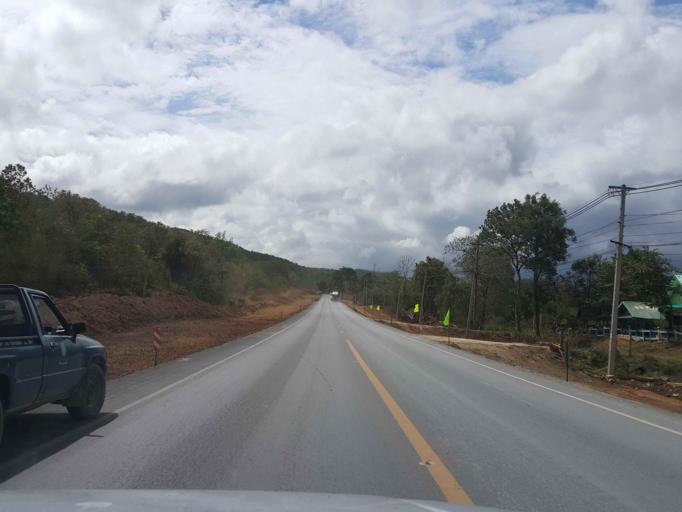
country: TH
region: Tak
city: Tak
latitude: 16.7978
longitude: 99.0079
